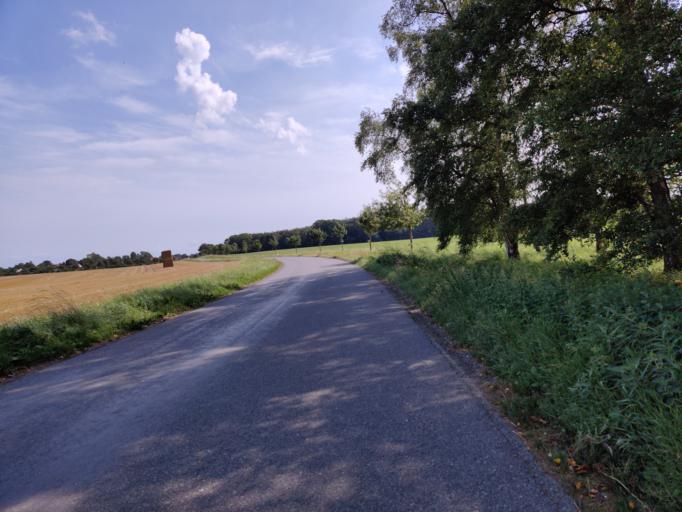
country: DK
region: Zealand
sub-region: Guldborgsund Kommune
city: Nykobing Falster
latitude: 54.6487
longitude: 11.8879
